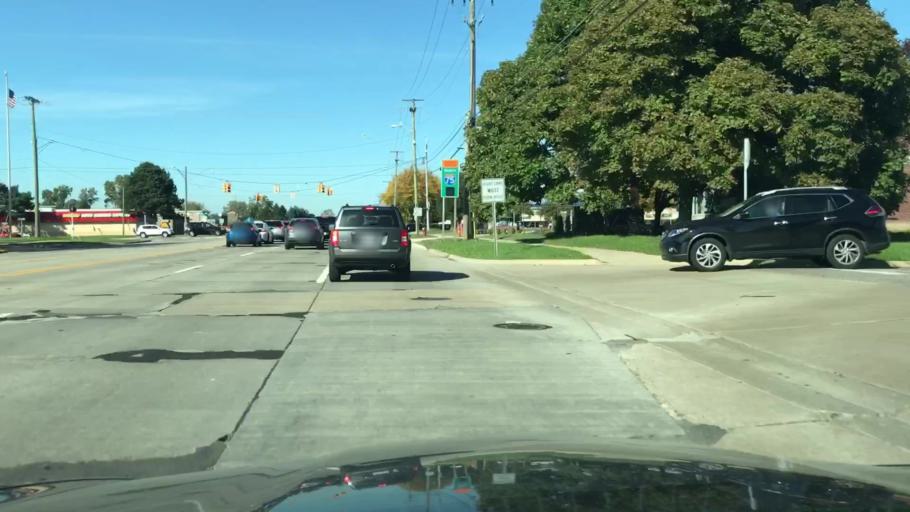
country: US
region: Michigan
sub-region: Macomb County
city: Sterling Heights
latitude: 42.5627
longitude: -83.0886
